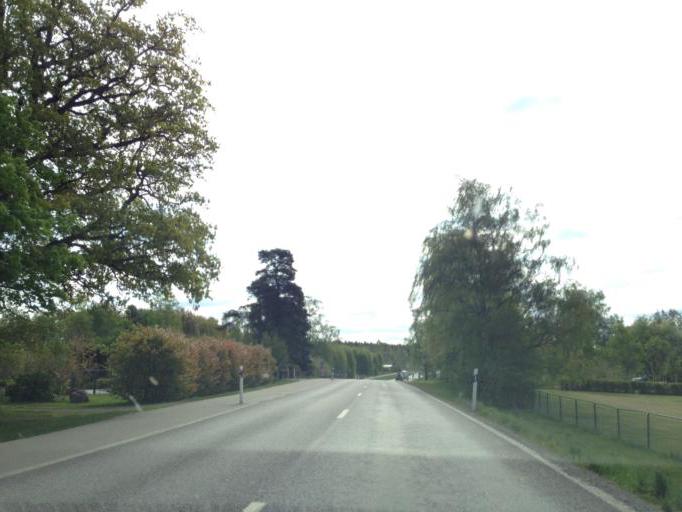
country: SE
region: Soedermanland
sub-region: Nykopings Kommun
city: Stigtomta
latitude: 58.8718
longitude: 16.8924
